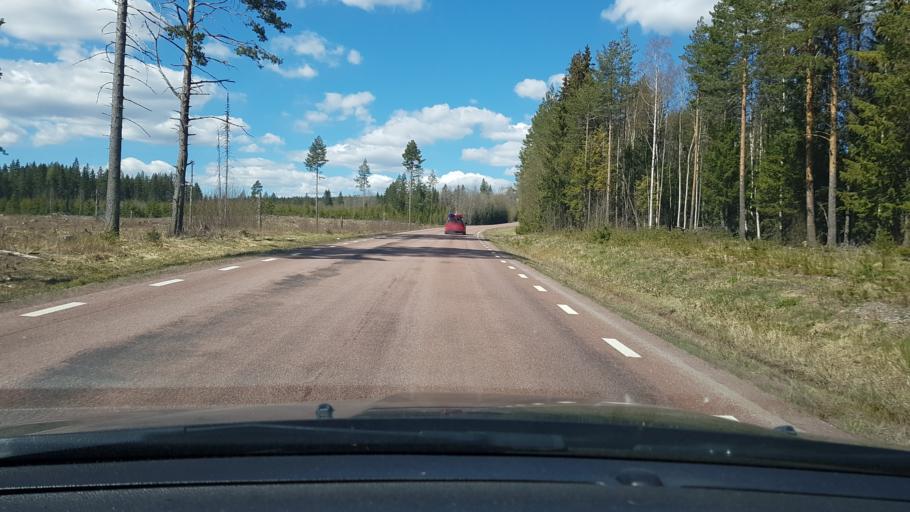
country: SE
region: Dalarna
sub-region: Alvdalens Kommun
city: AElvdalen
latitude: 61.1233
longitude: 13.9798
